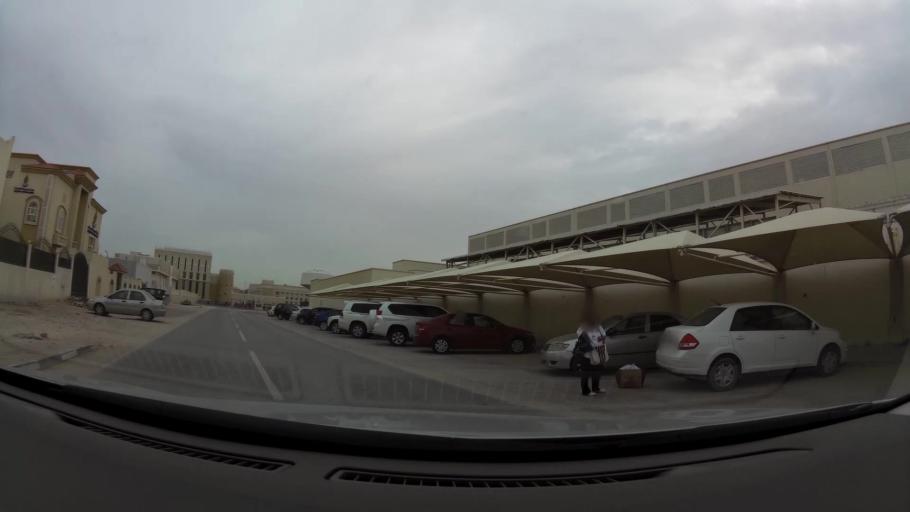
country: QA
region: Baladiyat ad Dawhah
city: Doha
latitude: 25.3080
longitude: 51.5014
